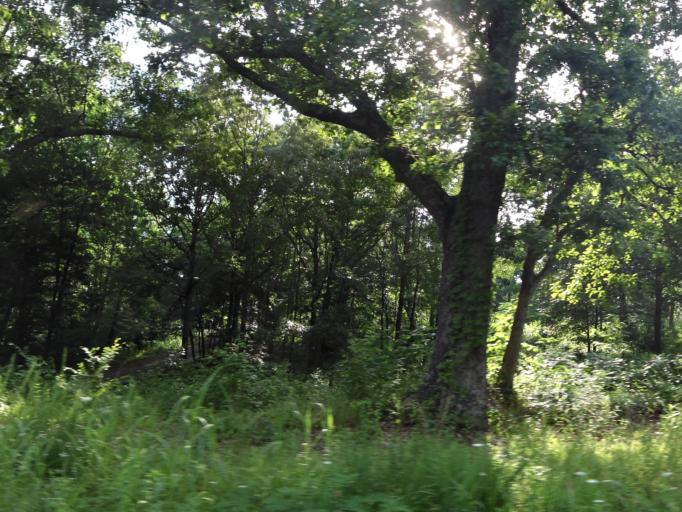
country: US
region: Tennessee
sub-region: Benton County
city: Camden
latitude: 36.0533
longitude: -88.1669
